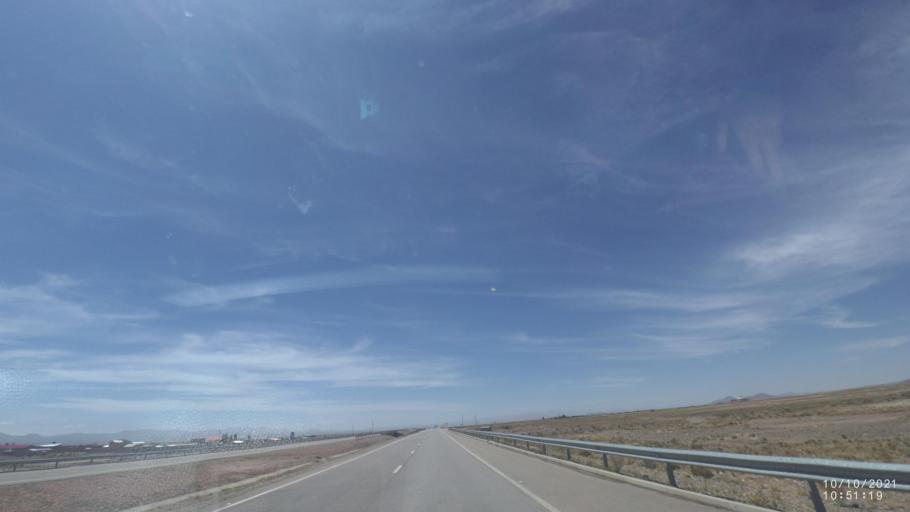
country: BO
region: La Paz
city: Colquiri
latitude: -17.6518
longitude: -67.2143
